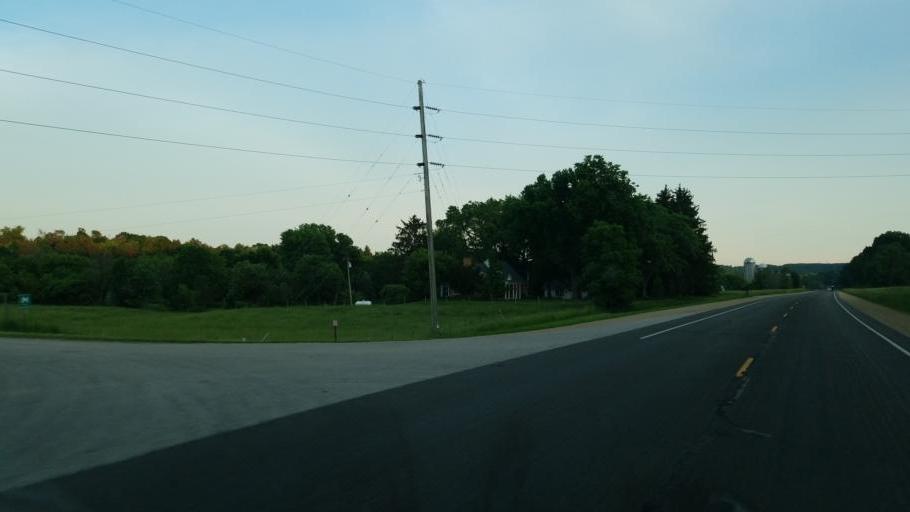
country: US
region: Wisconsin
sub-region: Monroe County
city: Tomah
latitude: 43.9367
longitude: -90.5029
